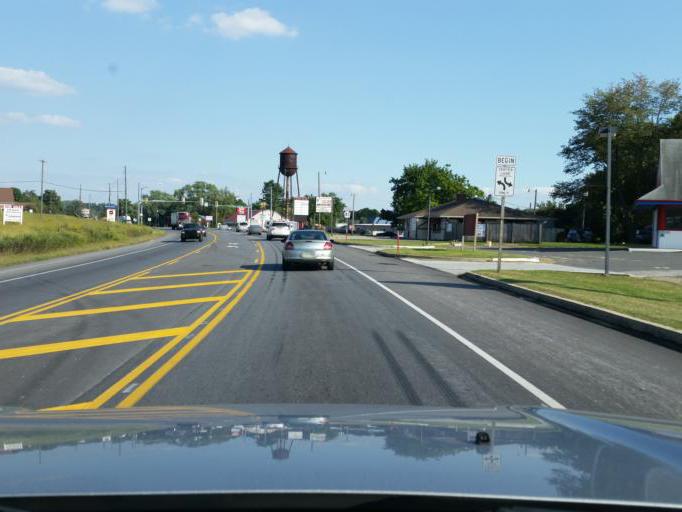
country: US
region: Pennsylvania
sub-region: Lancaster County
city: Christiana
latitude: 39.9637
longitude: -75.9993
